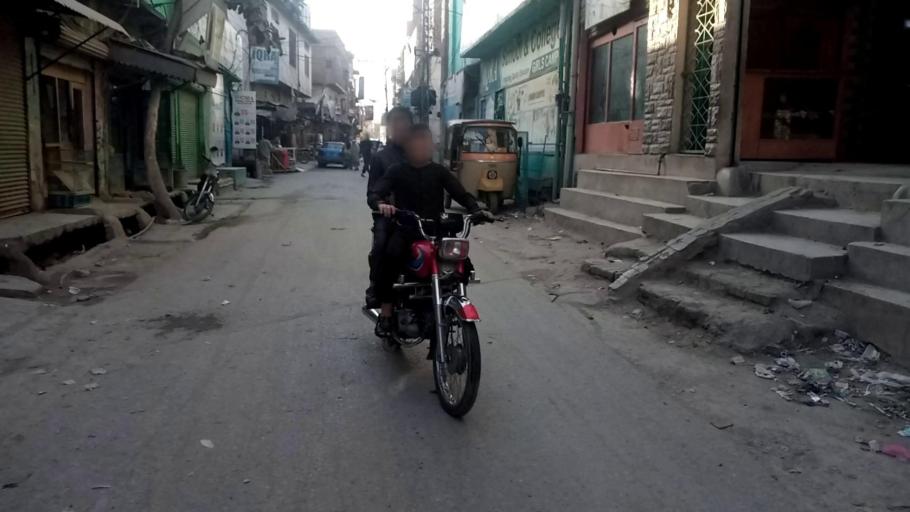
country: PK
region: Khyber Pakhtunkhwa
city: Peshawar
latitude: 34.0064
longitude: 71.5980
